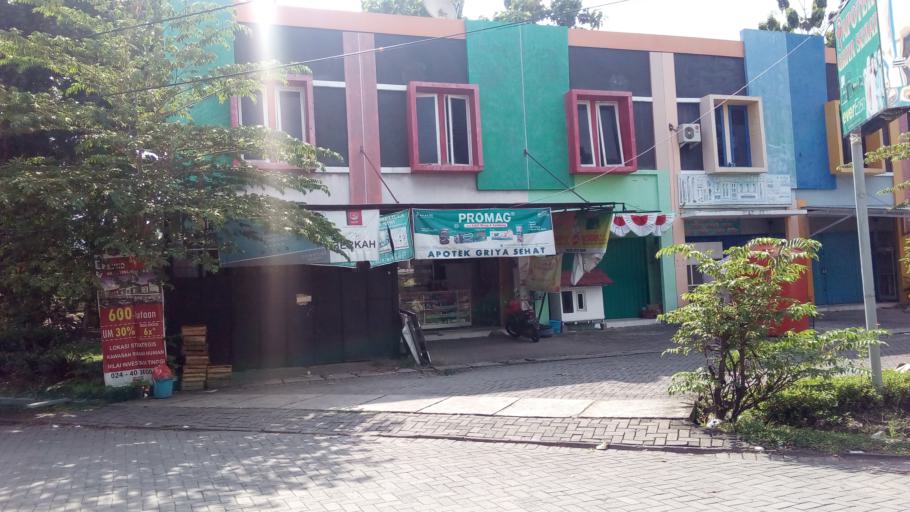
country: ID
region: Central Java
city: Mranggen
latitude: -7.0594
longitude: 110.4629
